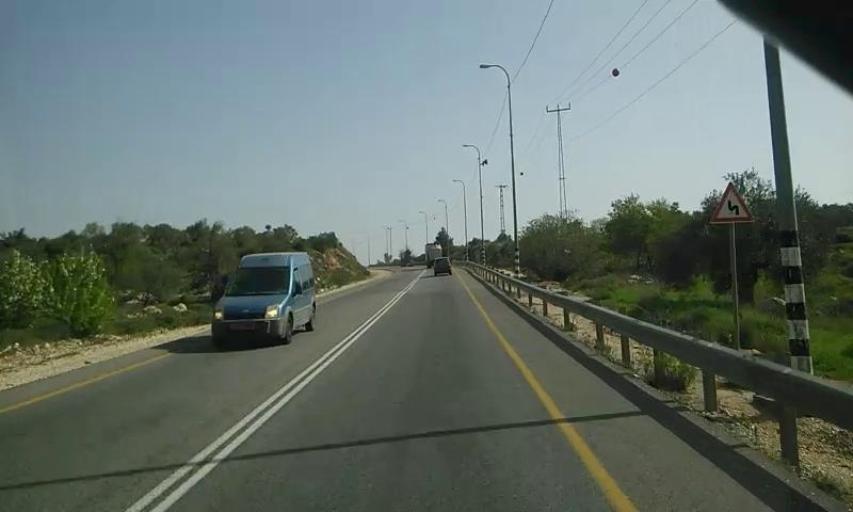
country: PS
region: West Bank
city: Turmus`ayya
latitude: 32.0428
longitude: 35.2821
